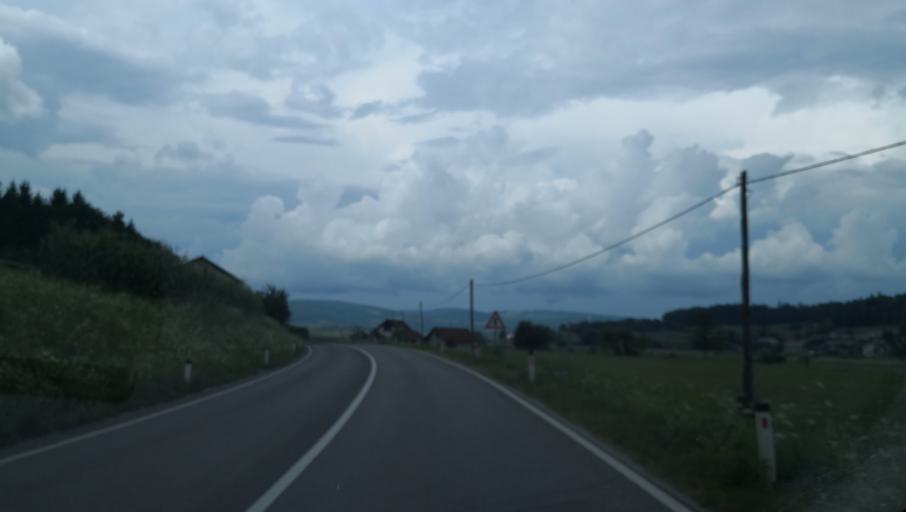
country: SI
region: Ivancna Gorica
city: Ivancna Gorica
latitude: 45.9134
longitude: 14.8020
